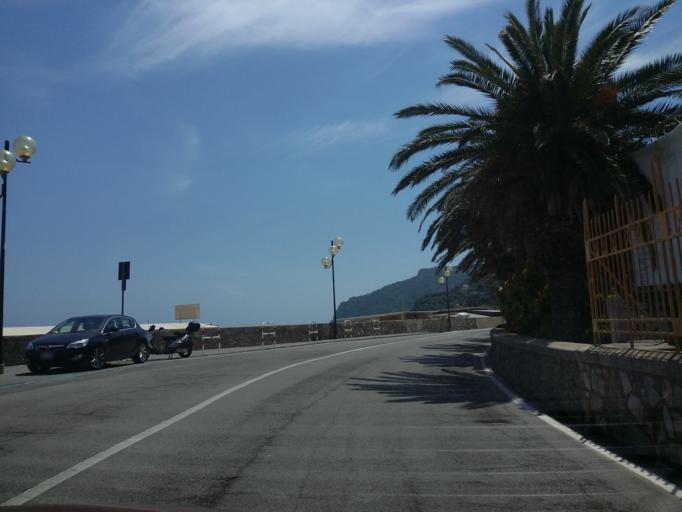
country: IT
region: Liguria
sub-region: Provincia di Savona
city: Spotorno
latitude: 44.2227
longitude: 8.4156
